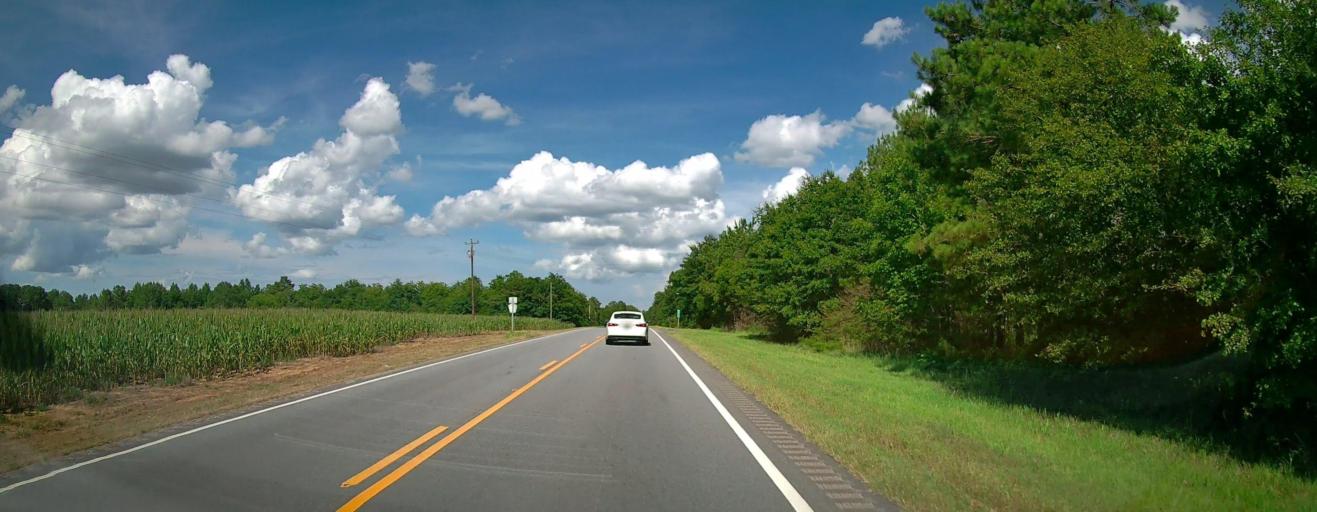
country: US
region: Alabama
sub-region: Lee County
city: Auburn
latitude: 32.4321
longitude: -85.4248
